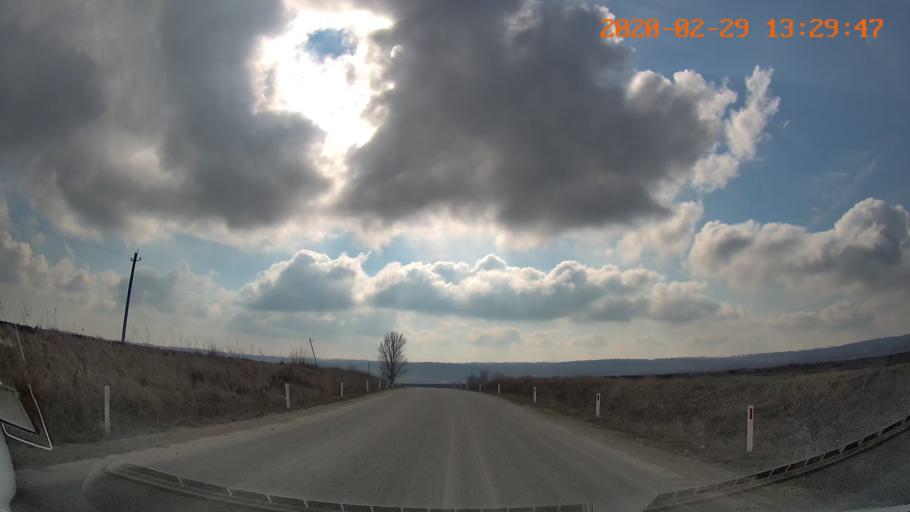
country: MD
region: Telenesti
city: Camenca
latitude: 47.8935
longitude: 28.6337
